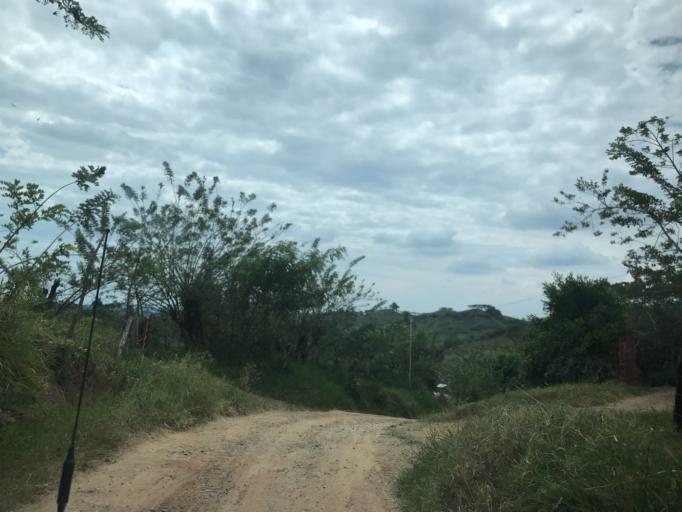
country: CO
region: Valle del Cauca
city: Obando
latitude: 4.5623
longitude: -75.9349
